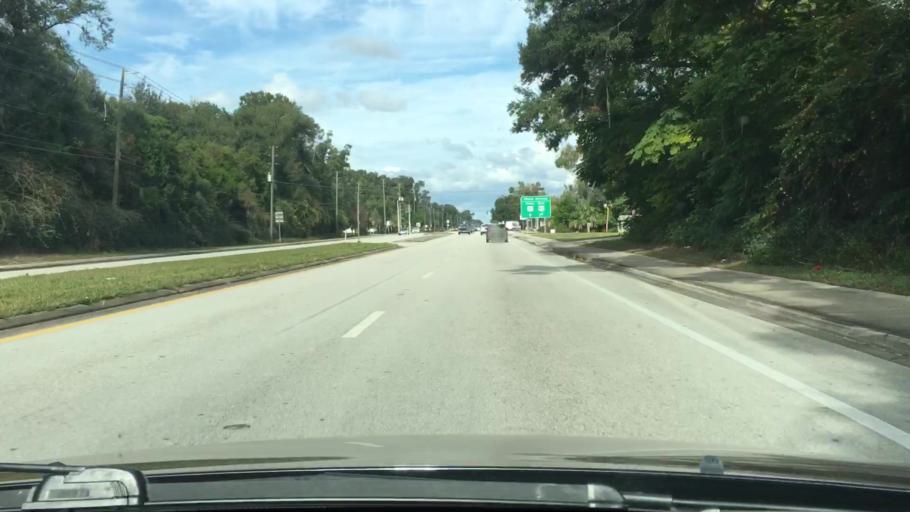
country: US
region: Florida
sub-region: Volusia County
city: North DeLand
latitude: 29.0521
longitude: -81.3249
